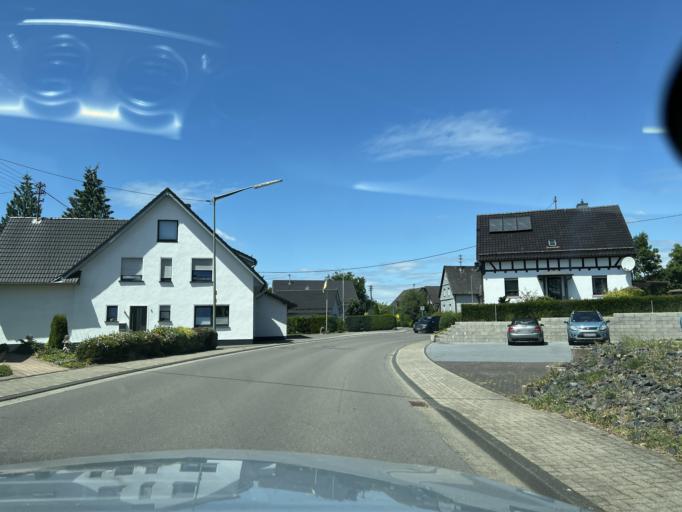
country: DE
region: North Rhine-Westphalia
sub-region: Regierungsbezirk Arnsberg
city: Wenden
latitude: 50.9403
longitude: 7.8880
